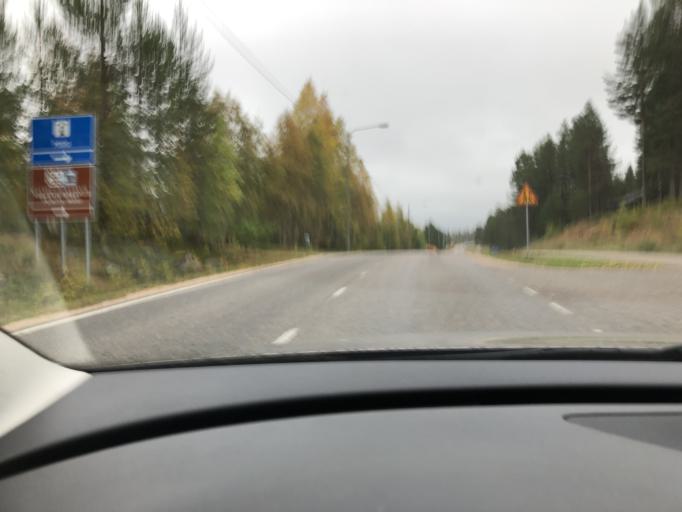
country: FI
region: Lapland
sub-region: Itae-Lappi
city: Posio
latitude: 66.1126
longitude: 28.1808
